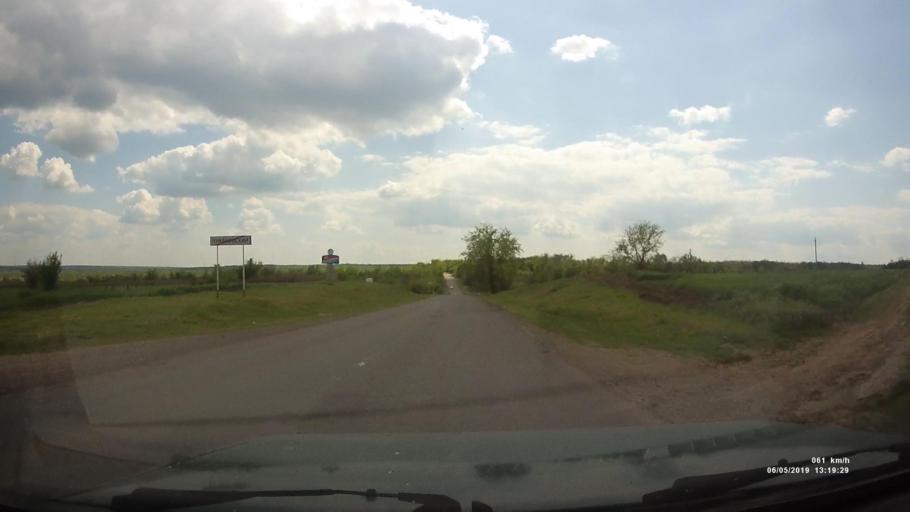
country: RU
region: Rostov
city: Ust'-Donetskiy
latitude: 47.7249
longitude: 40.9138
